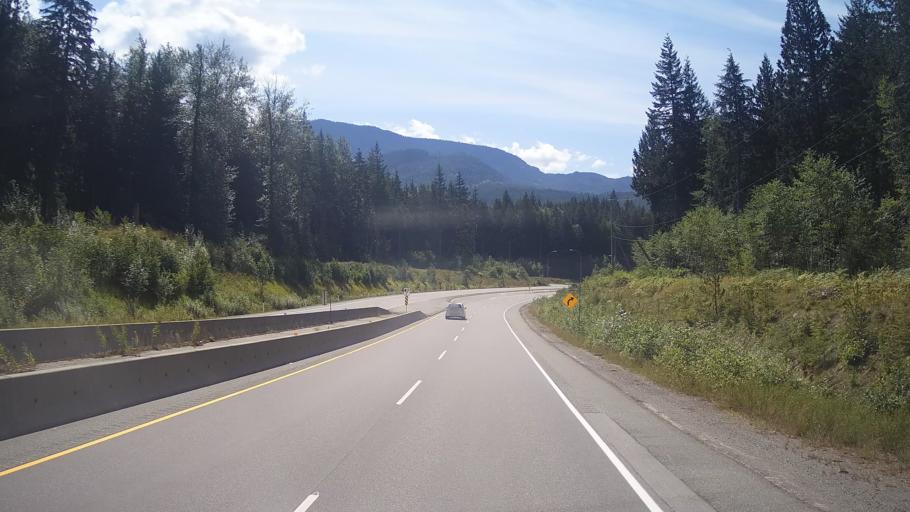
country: CA
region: British Columbia
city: Whistler
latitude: 49.9752
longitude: -123.1439
